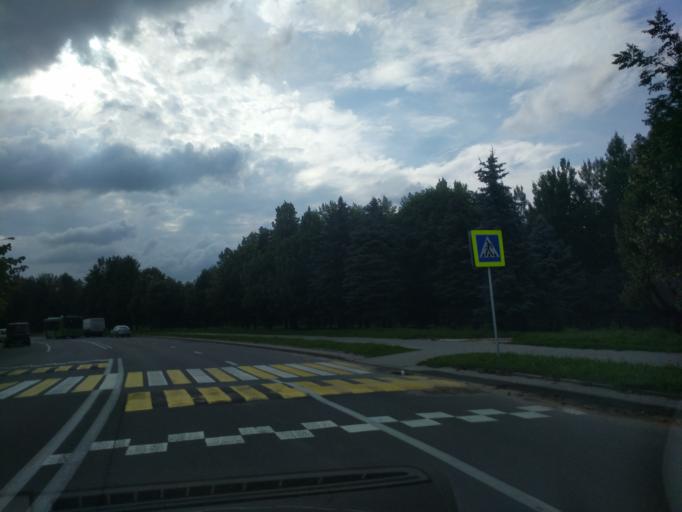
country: BY
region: Minsk
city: Malinovka
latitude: 53.8547
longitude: 27.4697
